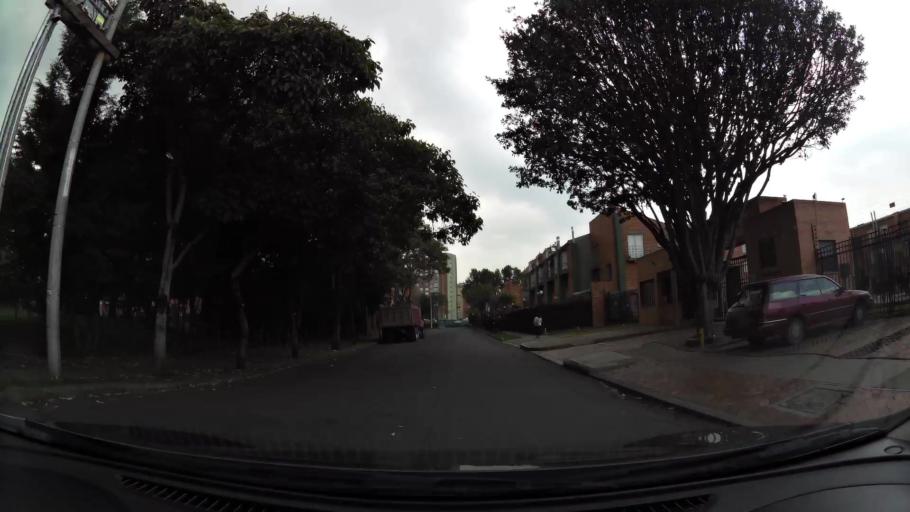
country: CO
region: Cundinamarca
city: Cota
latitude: 4.7446
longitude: -74.0554
